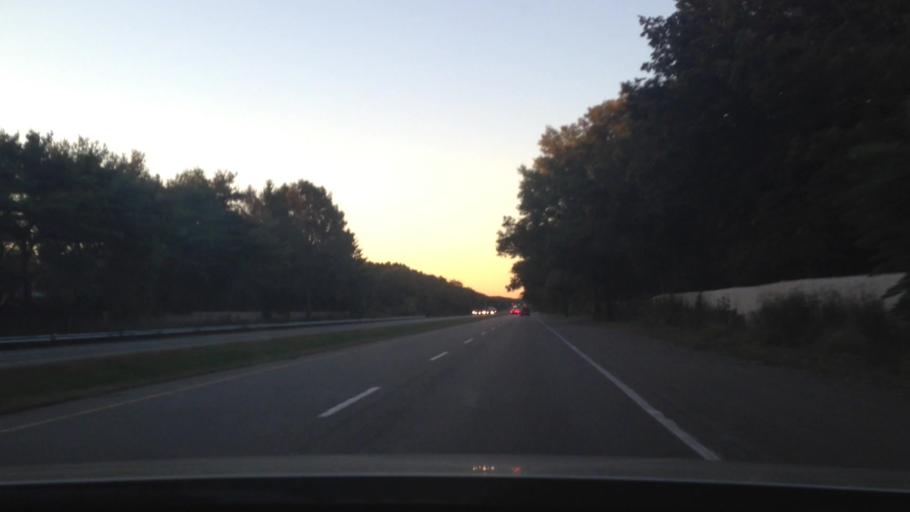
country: US
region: New York
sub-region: Suffolk County
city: Mount Sinai
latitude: 40.9193
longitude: -73.0079
